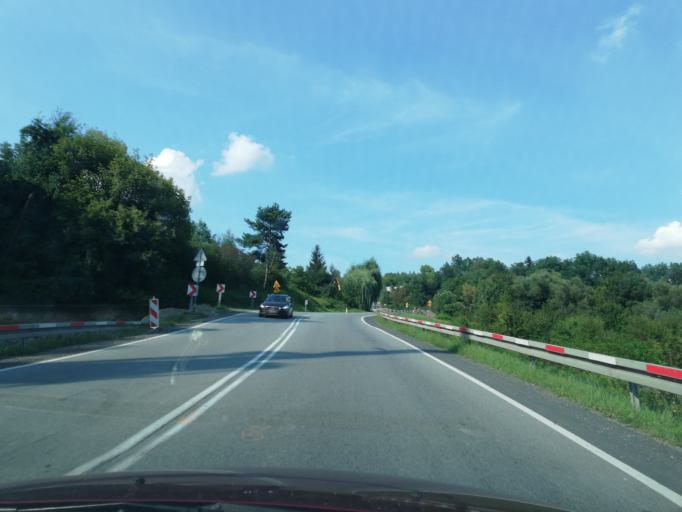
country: PL
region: Lesser Poland Voivodeship
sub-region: Powiat nowosadecki
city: Lososina Dolna
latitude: 49.7197
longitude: 20.6420
